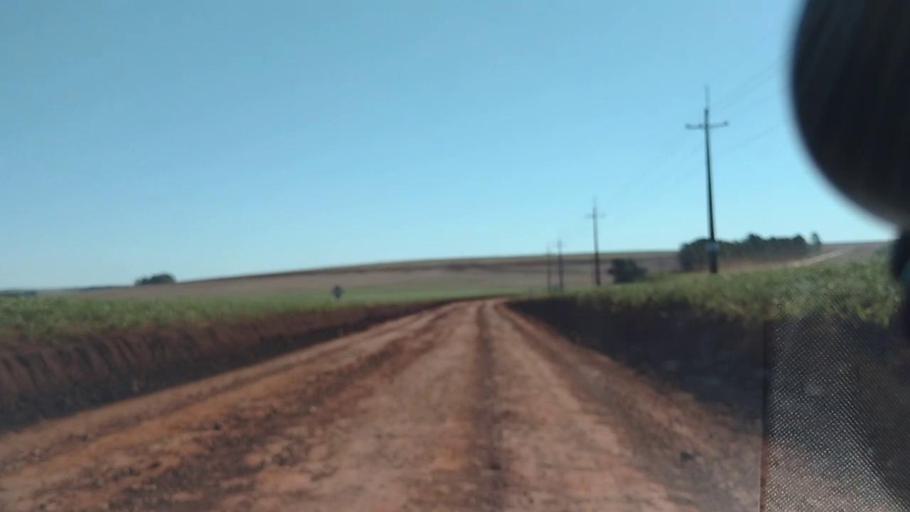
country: PY
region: Alto Parana
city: Naranjal
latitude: -25.9751
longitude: -55.2273
